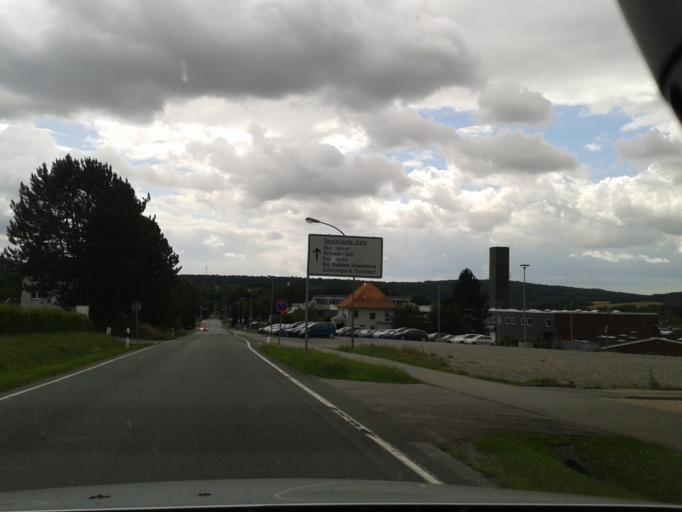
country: DE
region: North Rhine-Westphalia
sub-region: Regierungsbezirk Detmold
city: Blomberg
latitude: 51.9255
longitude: 9.1483
